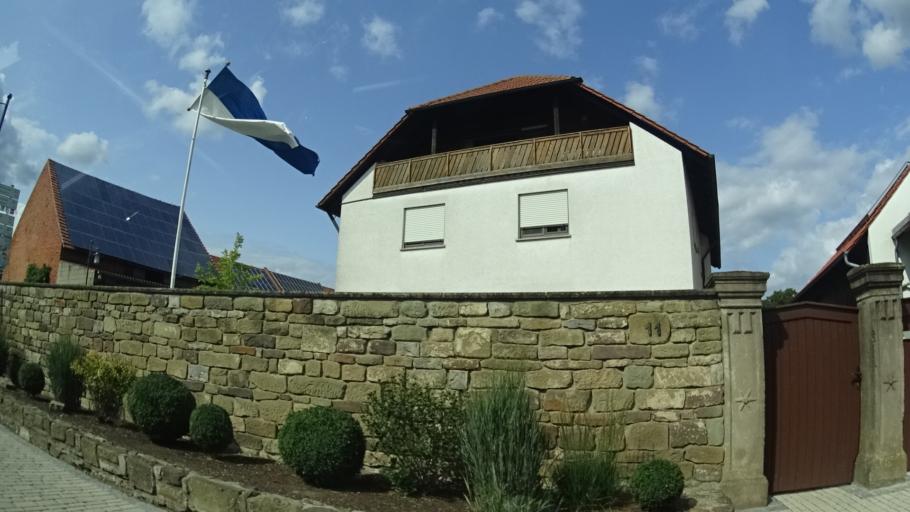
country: DE
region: Bavaria
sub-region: Regierungsbezirk Unterfranken
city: Bergrheinfeld
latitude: 50.0058
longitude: 10.1822
